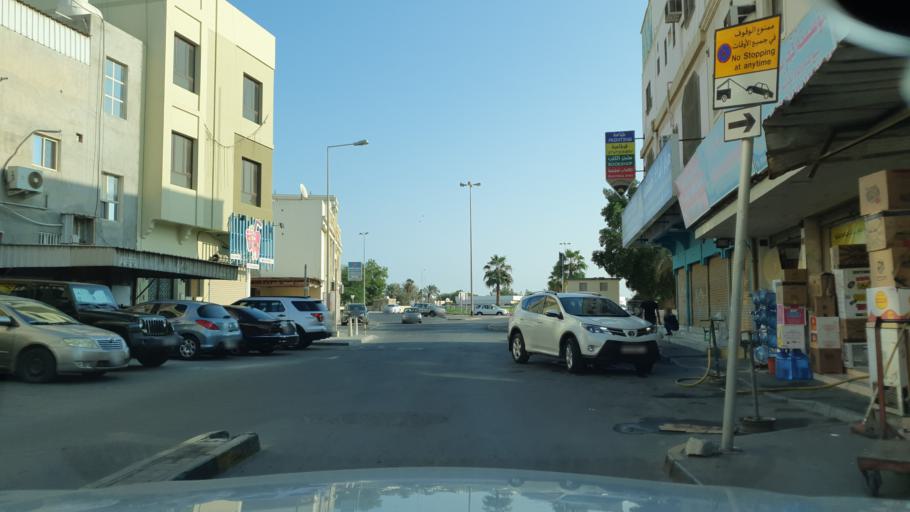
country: BH
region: Manama
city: Jidd Hafs
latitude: 26.2165
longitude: 50.4679
